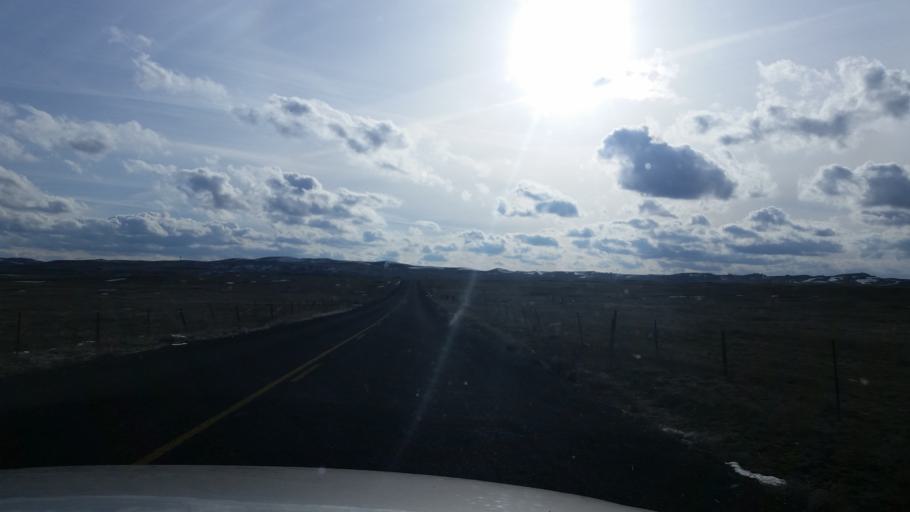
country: US
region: Washington
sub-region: Spokane County
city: Cheney
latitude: 47.2662
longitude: -117.6660
